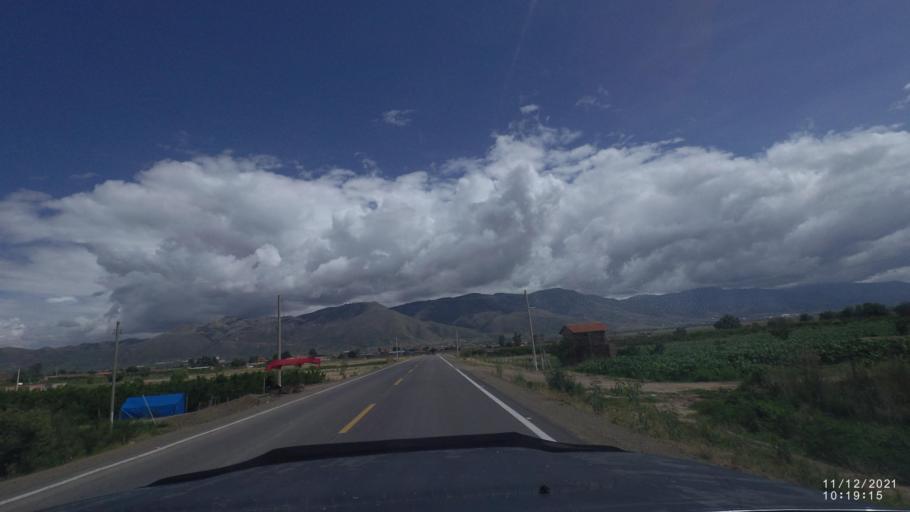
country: BO
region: Cochabamba
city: Tarata
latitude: -17.5726
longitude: -66.0098
